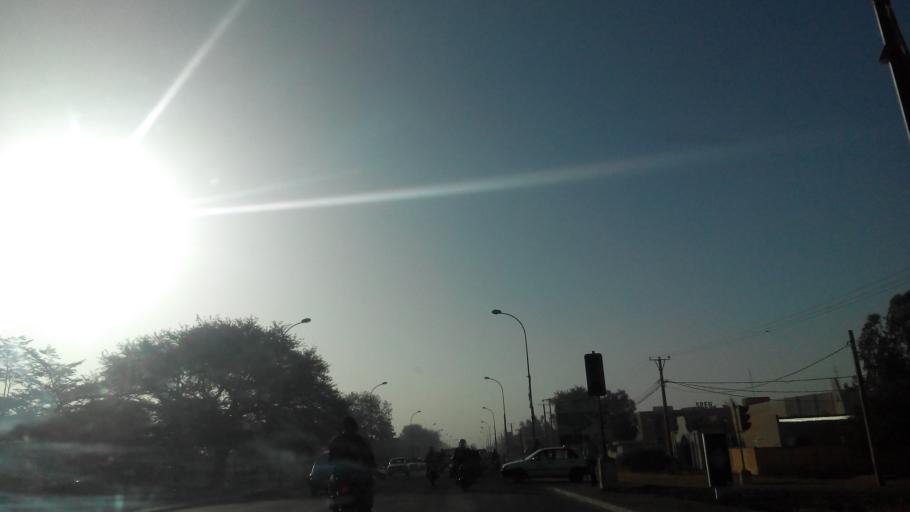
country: NE
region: Niamey
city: Niamey
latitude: 13.5380
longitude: 2.0762
